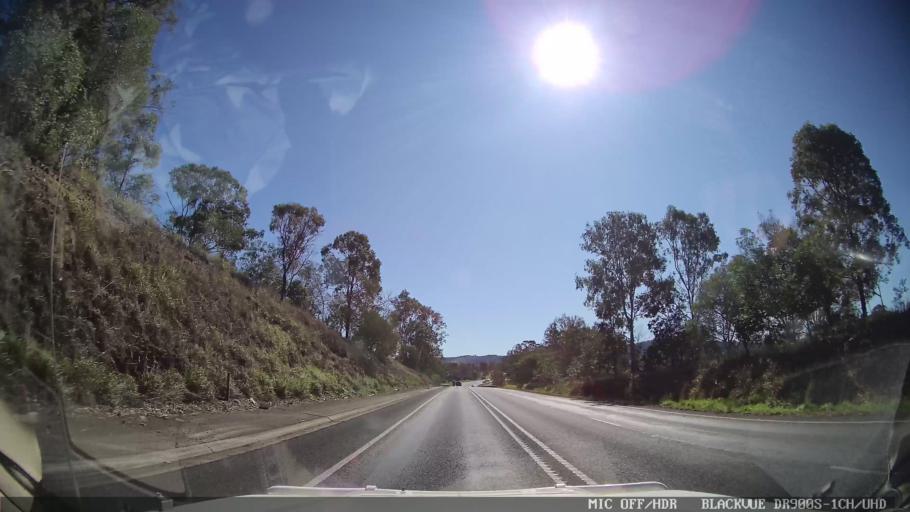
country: AU
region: Queensland
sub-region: Gympie Regional Council
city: Gympie
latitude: -25.9993
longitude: 152.5664
